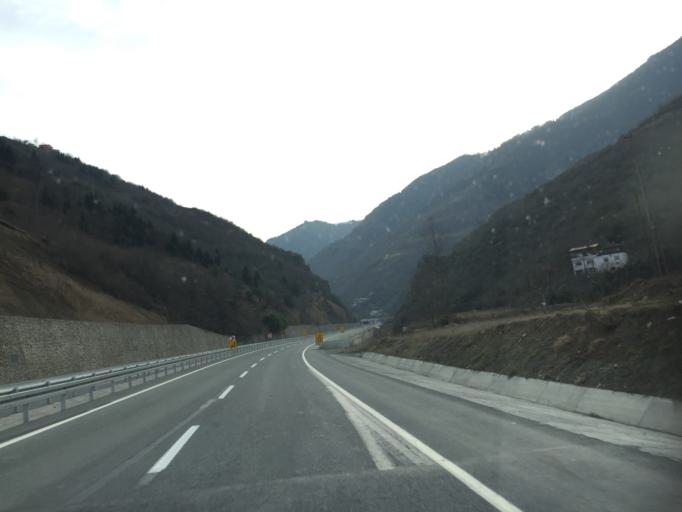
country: TR
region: Trabzon
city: Macka
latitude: 40.7863
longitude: 39.5772
